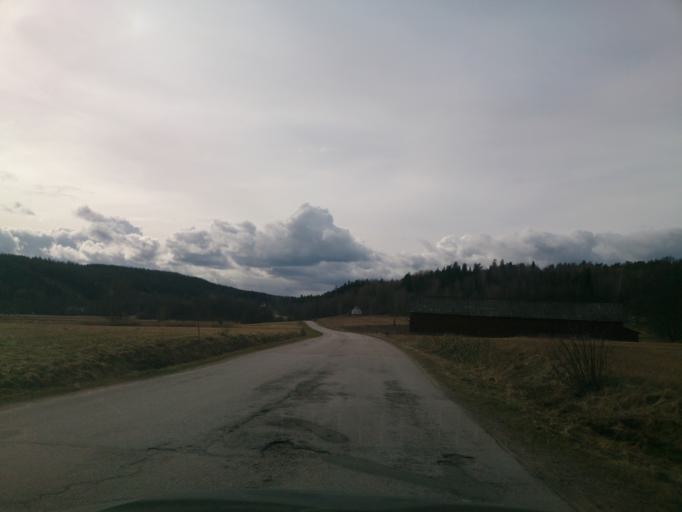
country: SE
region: OEstergoetland
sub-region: Norrkopings Kommun
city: Jursla
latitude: 58.6728
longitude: 16.1535
